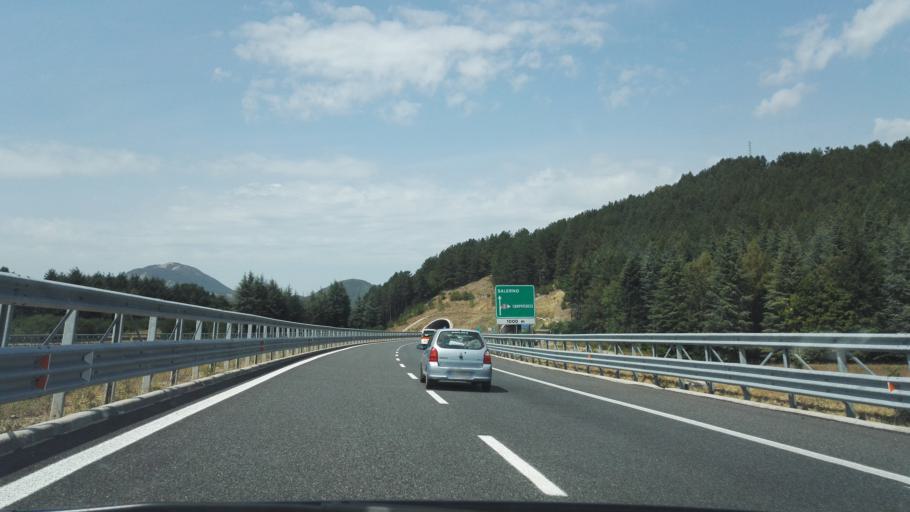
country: IT
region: Calabria
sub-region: Provincia di Cosenza
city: Morano Calabro
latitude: 39.8637
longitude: 16.0863
